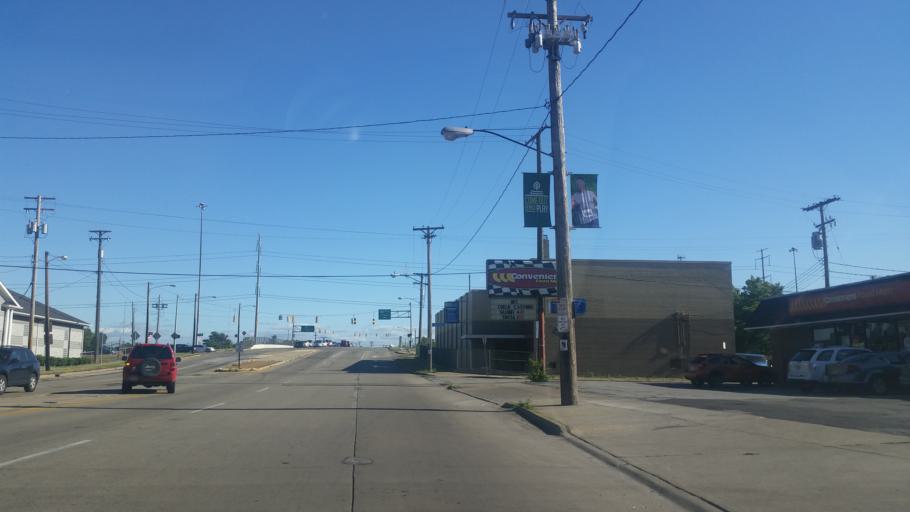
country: US
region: Ohio
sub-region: Cuyahoga County
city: Brooklyn Heights
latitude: 41.4233
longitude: -81.7099
